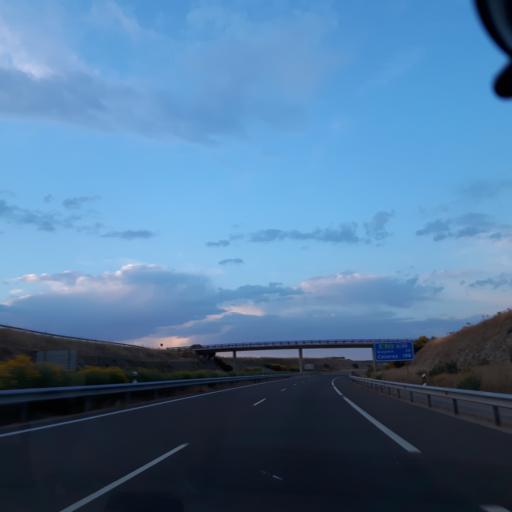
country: ES
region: Castille and Leon
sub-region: Provincia de Salamanca
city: Mozarbez
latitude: 40.8618
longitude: -5.6438
